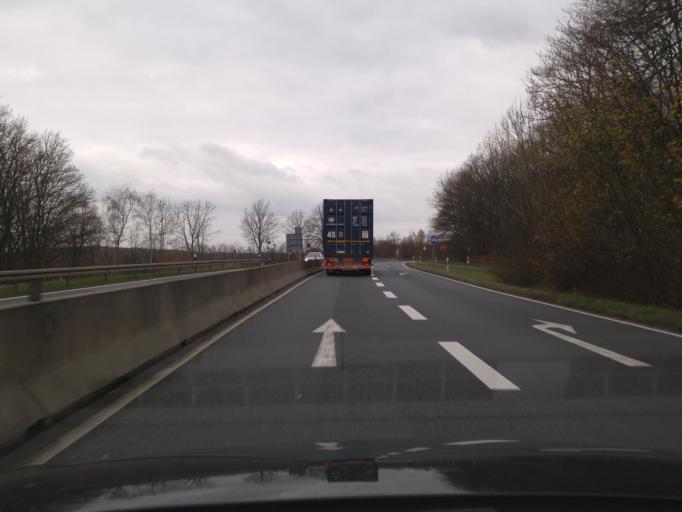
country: DE
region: Lower Saxony
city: Holle
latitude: 52.1045
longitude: 10.1505
